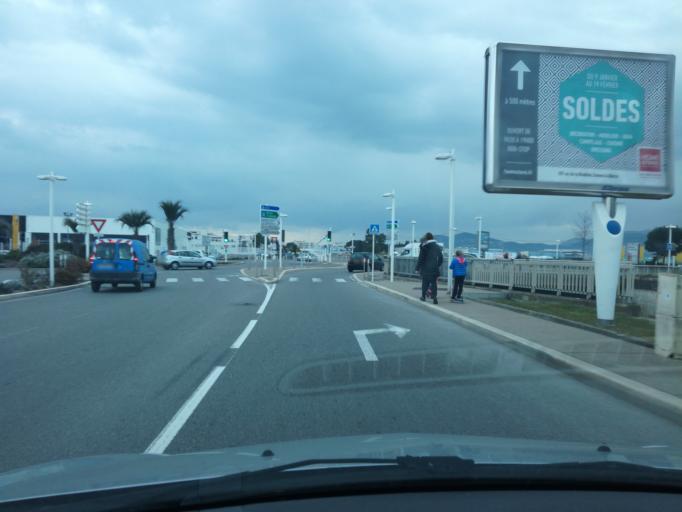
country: FR
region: Provence-Alpes-Cote d'Azur
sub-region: Departement des Alpes-Maritimes
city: Mandelieu-la-Napoule
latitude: 43.5507
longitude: 6.9621
